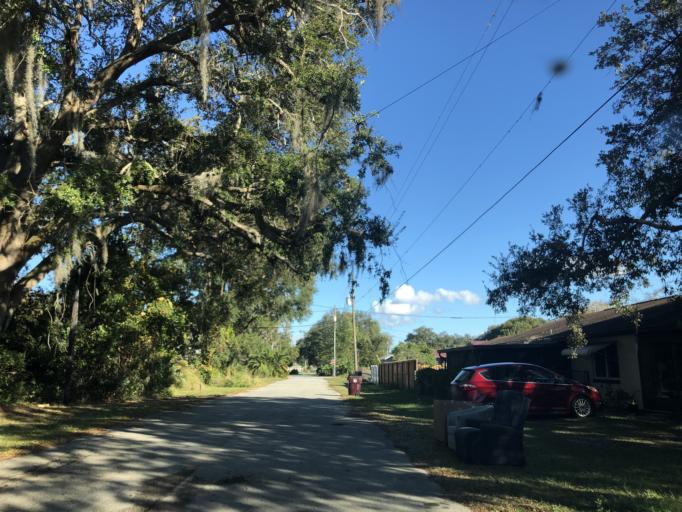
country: US
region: Florida
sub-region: Osceola County
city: Saint Cloud
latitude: 28.2516
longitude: -81.2970
